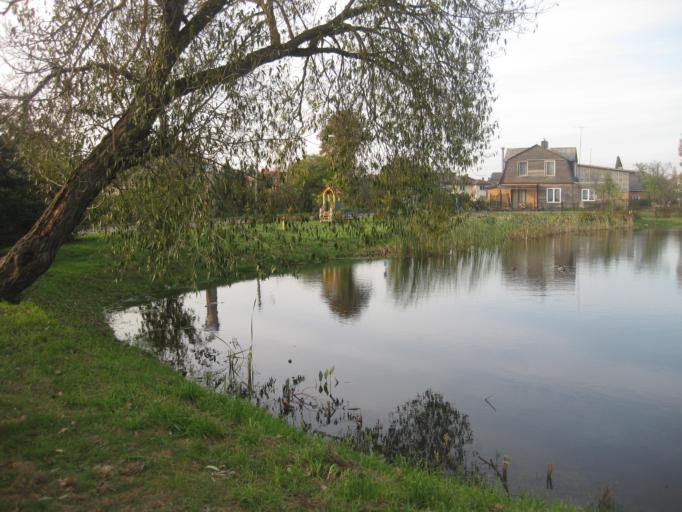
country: LT
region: Kauno apskritis
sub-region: Kaunas
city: Aleksotas
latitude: 54.8889
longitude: 23.8758
